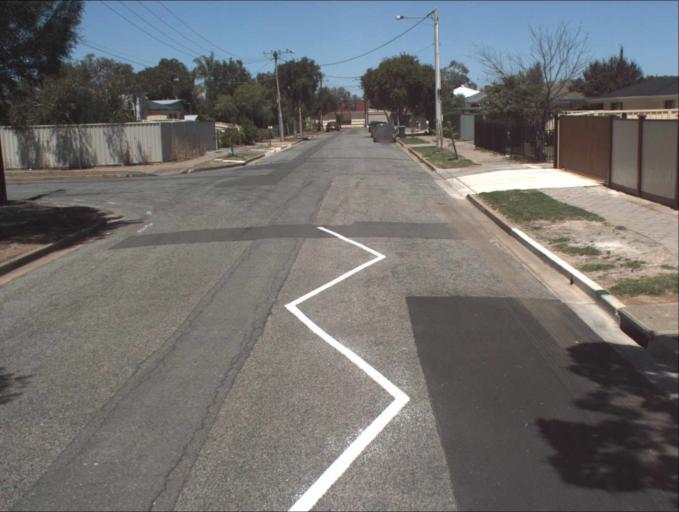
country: AU
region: South Australia
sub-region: Port Adelaide Enfield
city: Klemzig
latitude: -34.8683
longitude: 138.6285
